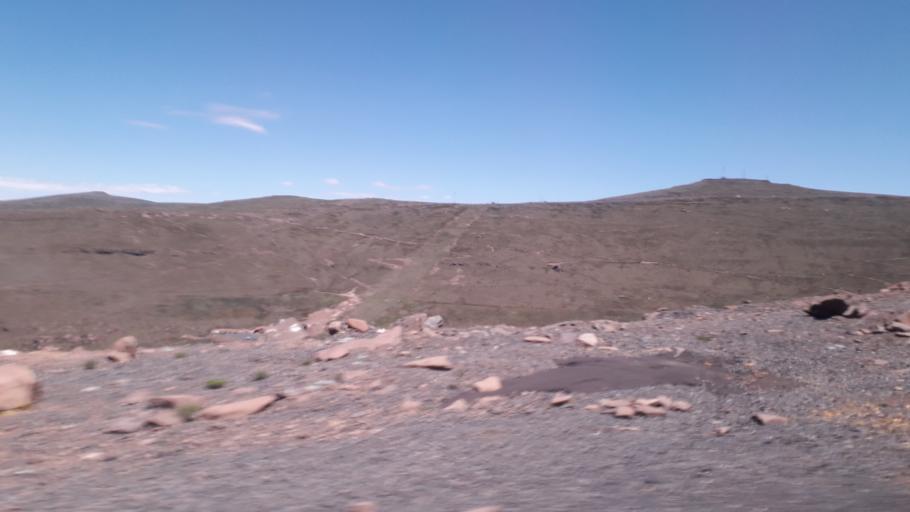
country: ZA
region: Orange Free State
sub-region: Thabo Mofutsanyana District Municipality
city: Phuthaditjhaba
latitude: -28.8250
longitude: 28.7328
